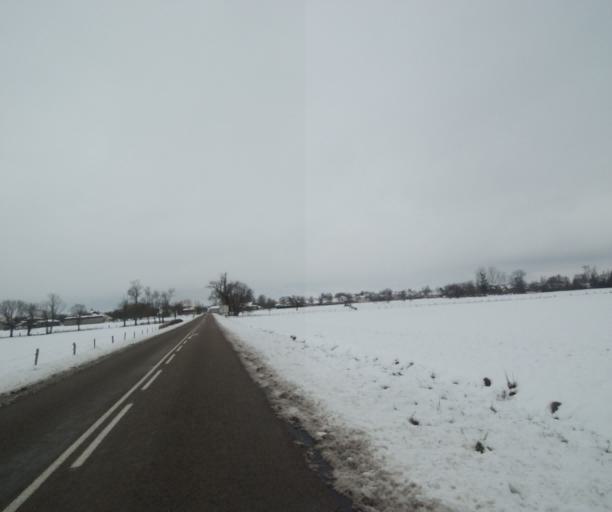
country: FR
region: Champagne-Ardenne
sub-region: Departement de la Haute-Marne
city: Montier-en-Der
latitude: 48.4772
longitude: 4.7869
